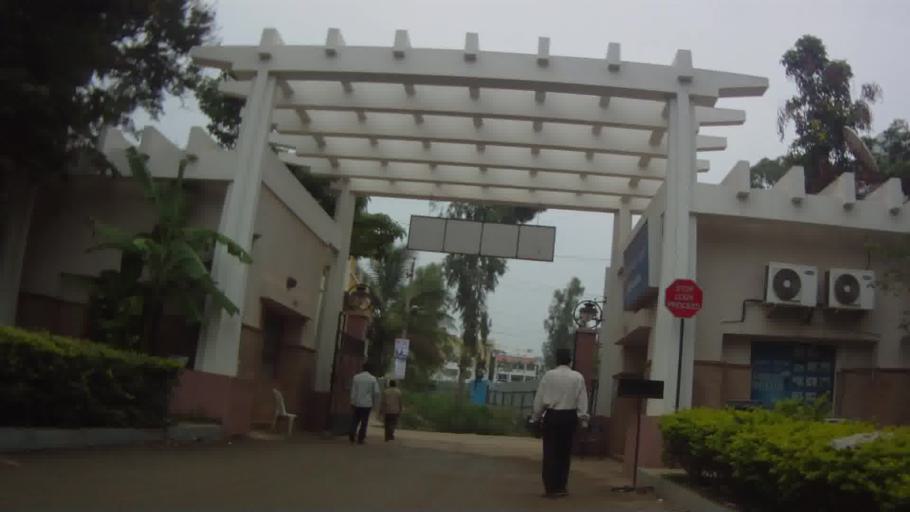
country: IN
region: Karnataka
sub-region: Bangalore Rural
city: Hoskote
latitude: 12.9628
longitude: 77.7505
